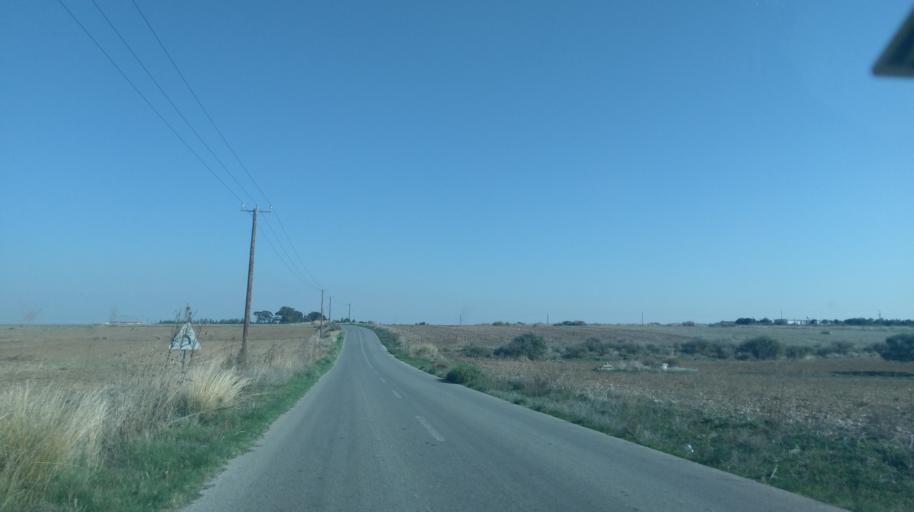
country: CY
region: Larnaka
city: Athienou
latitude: 35.1610
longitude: 33.5144
